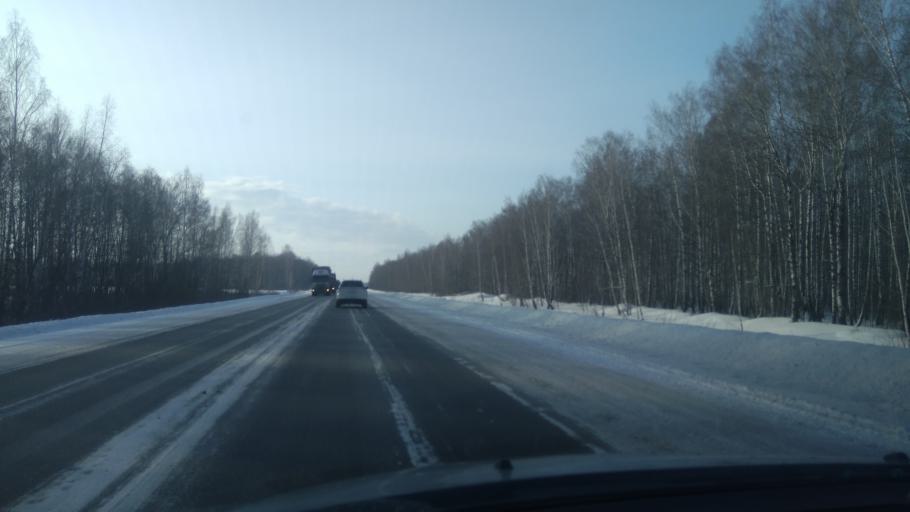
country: RU
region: Sverdlovsk
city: Bogdanovich
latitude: 56.8059
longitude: 62.0298
